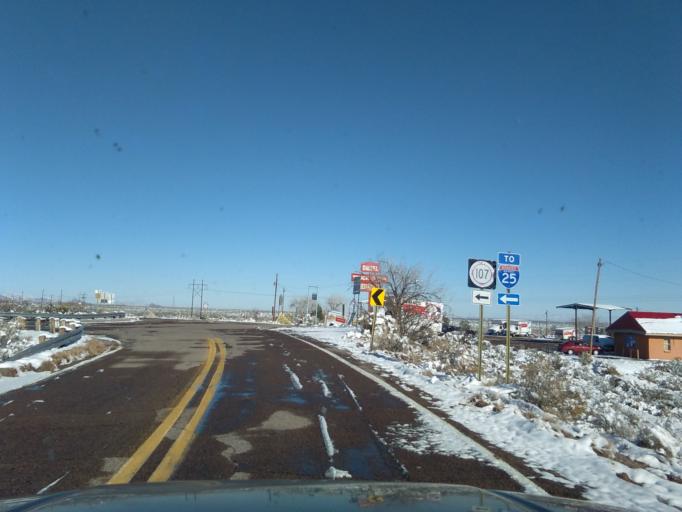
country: US
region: New Mexico
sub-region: Socorro County
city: Socorro
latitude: 33.6356
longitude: -107.1200
